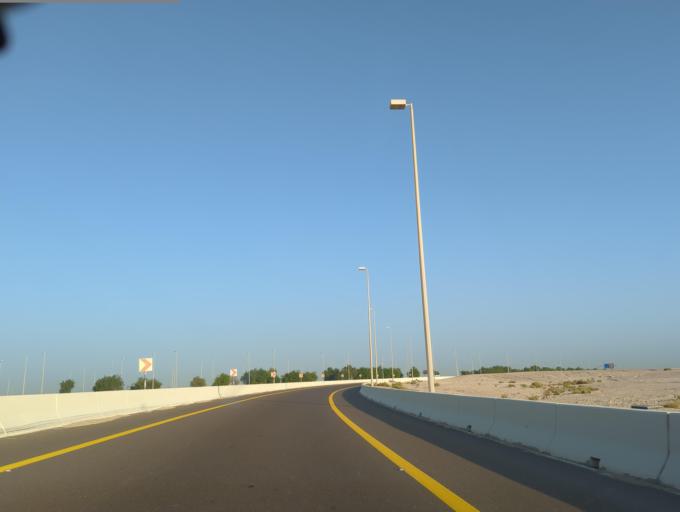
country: AE
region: Abu Dhabi
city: Abu Dhabi
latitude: 24.4127
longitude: 54.6773
